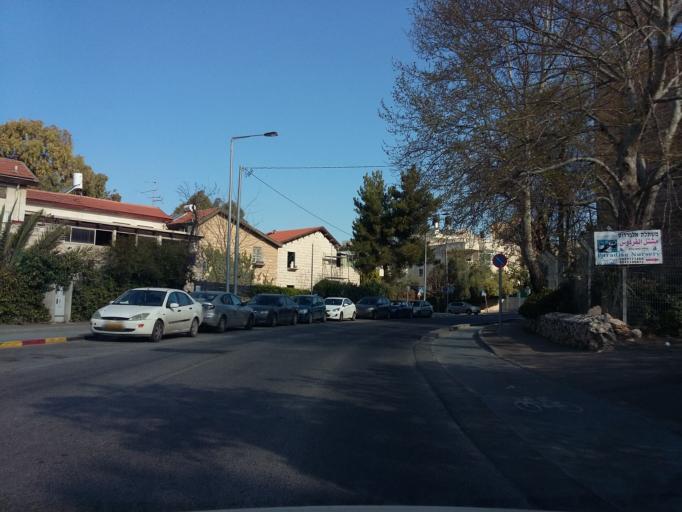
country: PS
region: West Bank
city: East Jerusalem
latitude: 31.7989
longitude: 35.2361
